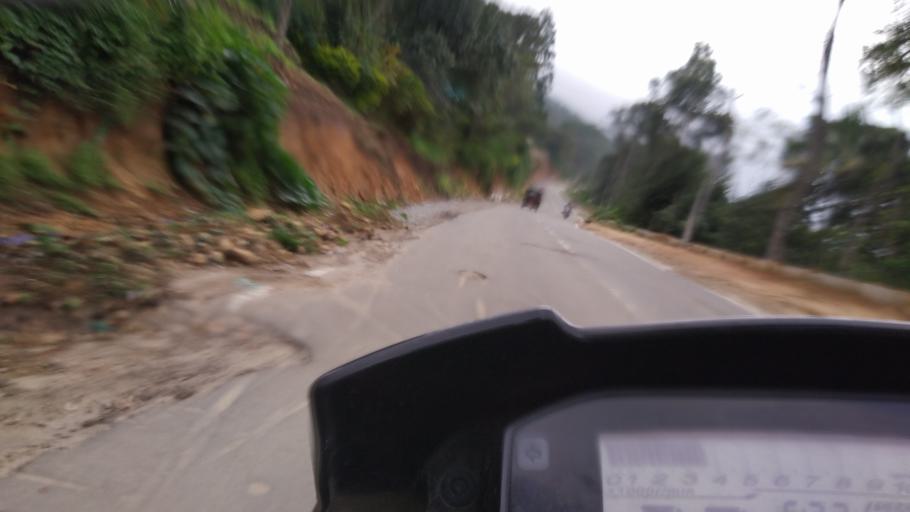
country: IN
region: Tamil Nadu
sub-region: Theni
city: Bodinayakkanur
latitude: 10.0114
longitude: 77.2368
